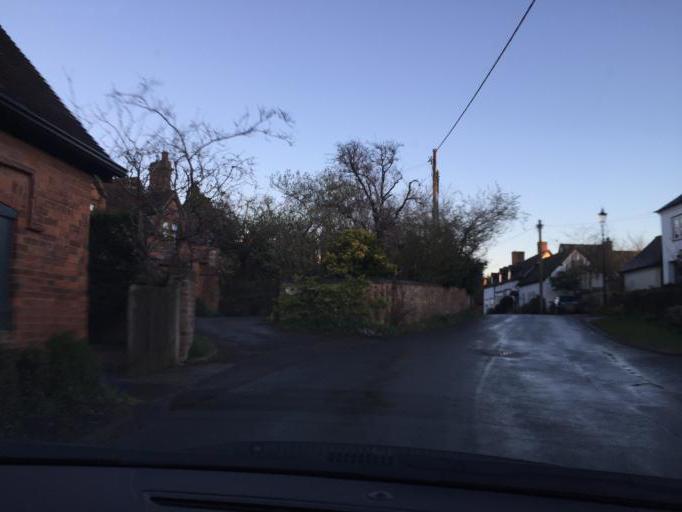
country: GB
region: England
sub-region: Warwickshire
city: Wroxall
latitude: 52.2667
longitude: -1.6685
